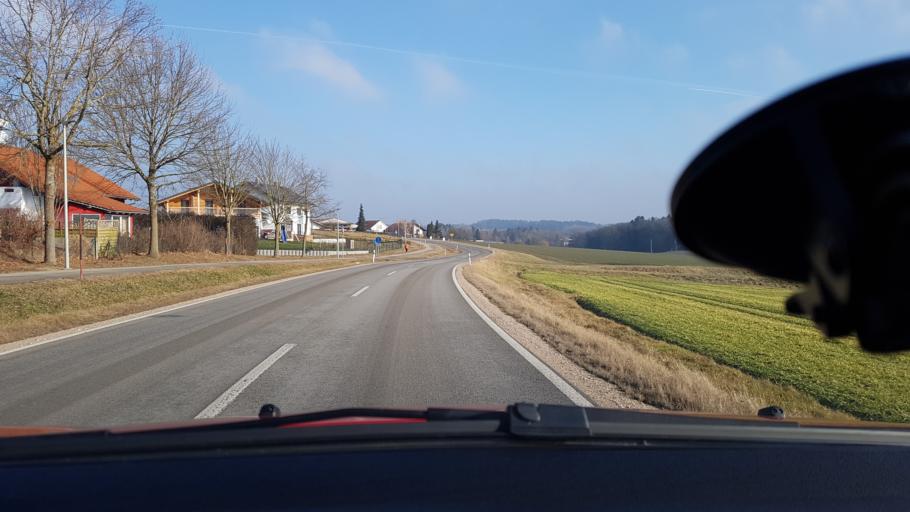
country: DE
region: Bavaria
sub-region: Lower Bavaria
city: Wittibreut
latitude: 48.3257
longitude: 12.9846
